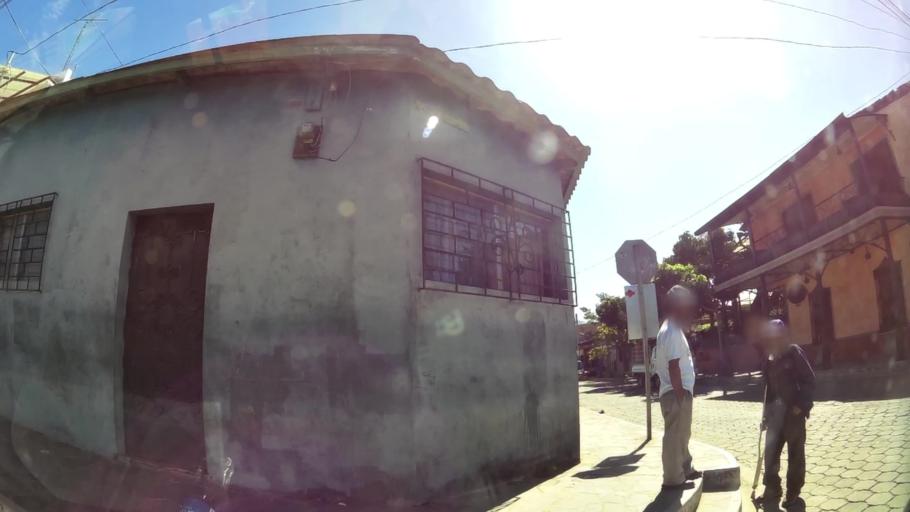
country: SV
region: Ahuachapan
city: Concepcion de Ataco
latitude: 13.8691
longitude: -89.8516
